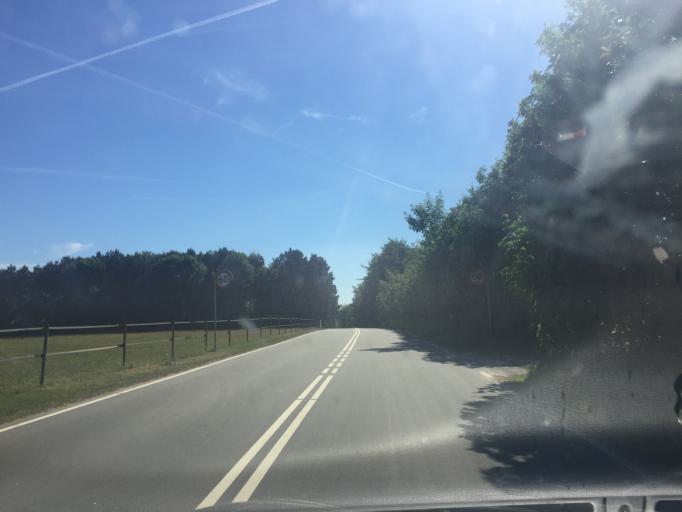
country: DK
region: Capital Region
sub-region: Hoje-Taastrup Kommune
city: Flong
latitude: 55.6675
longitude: 12.2285
